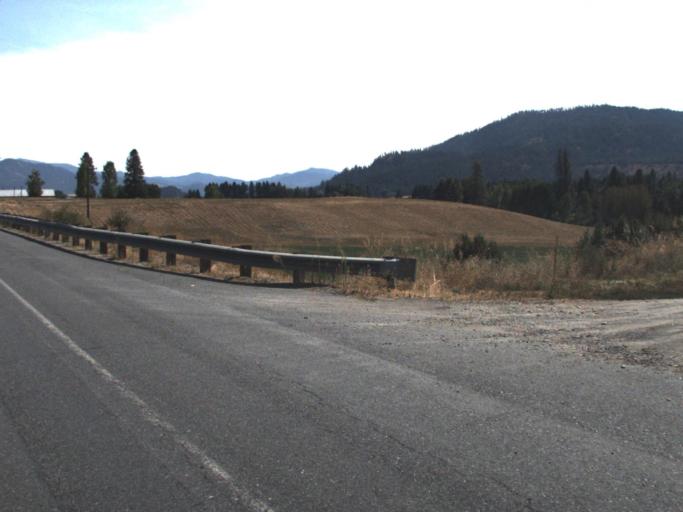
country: US
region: Washington
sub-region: Stevens County
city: Chewelah
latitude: 48.3169
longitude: -117.8137
